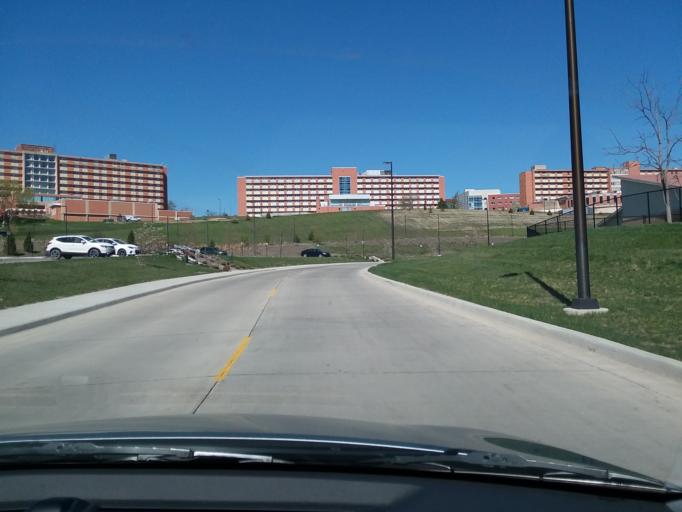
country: US
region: Kansas
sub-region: Douglas County
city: Lawrence
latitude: 38.9528
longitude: -95.2558
